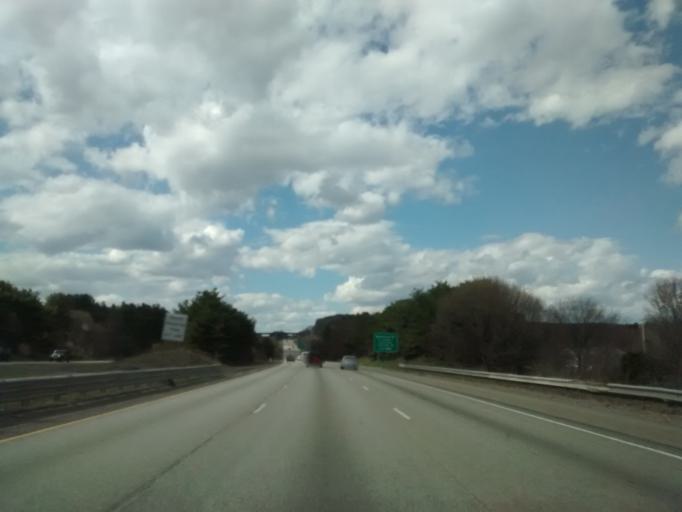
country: US
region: Massachusetts
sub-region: Middlesex County
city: Marlborough
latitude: 42.3082
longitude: -71.5656
